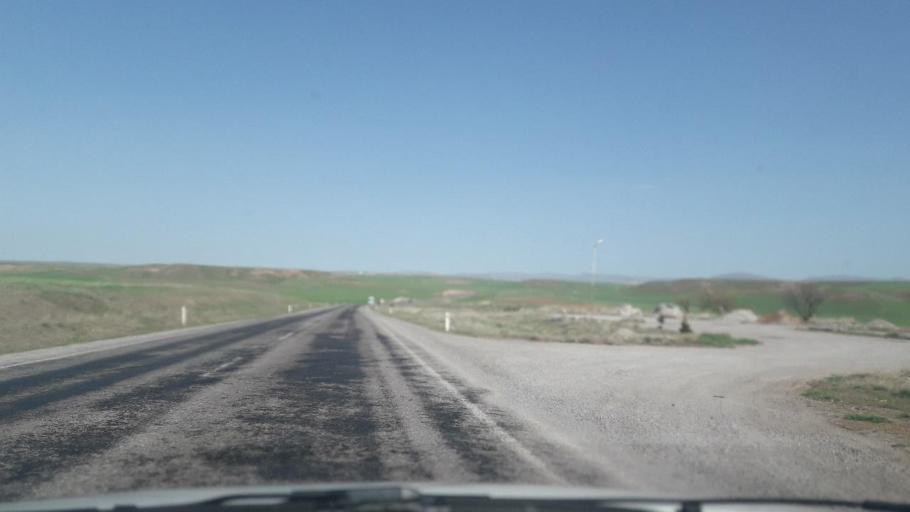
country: TR
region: Sivas
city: Kangal
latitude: 39.1872
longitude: 37.4290
